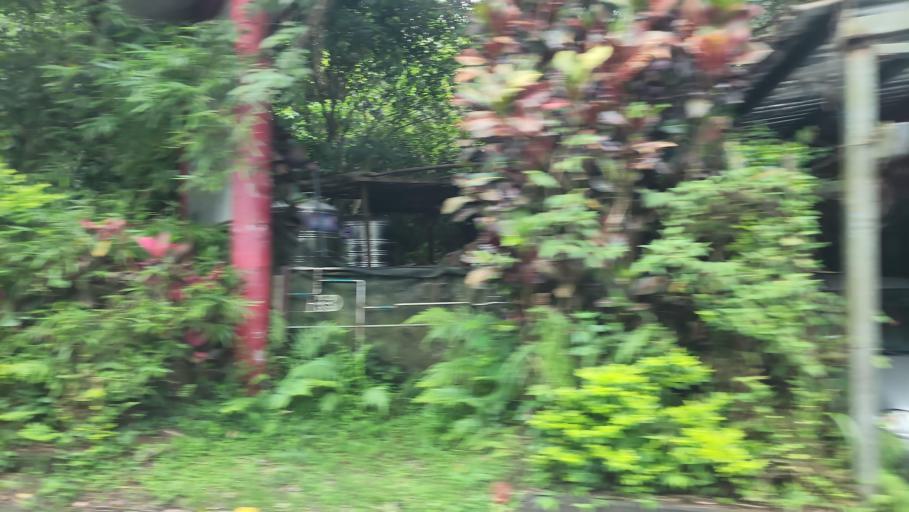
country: TW
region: Taiwan
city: Daxi
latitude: 24.8728
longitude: 121.4045
